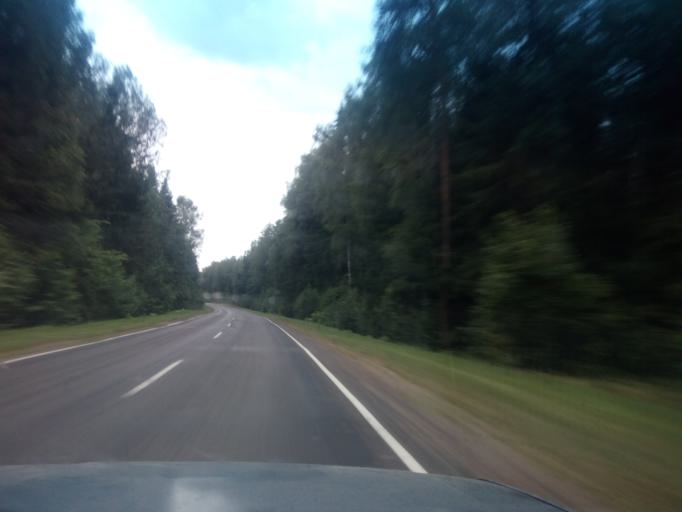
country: BY
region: Vitebsk
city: Dzisna
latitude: 55.6184
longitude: 28.4063
